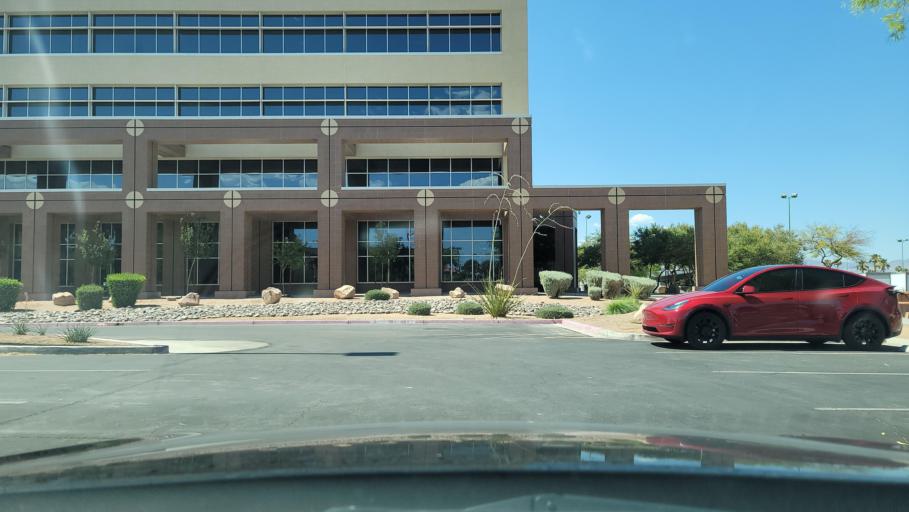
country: US
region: Nevada
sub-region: Clark County
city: Las Vegas
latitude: 36.1824
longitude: -115.1314
